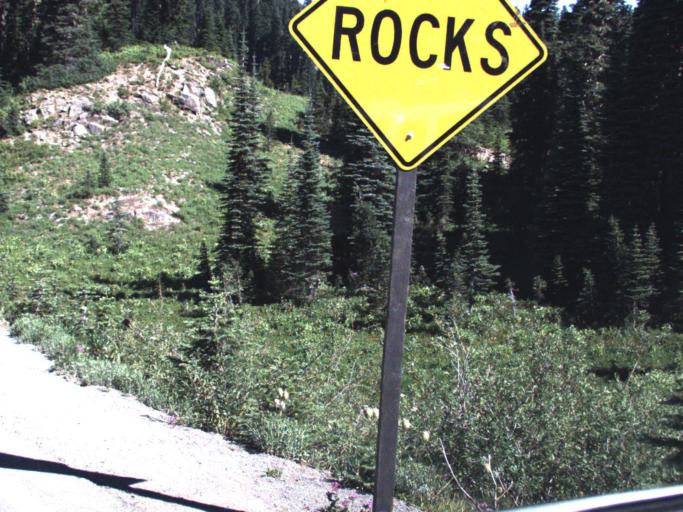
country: US
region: Washington
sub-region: King County
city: Enumclaw
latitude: 46.8673
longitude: -121.5185
